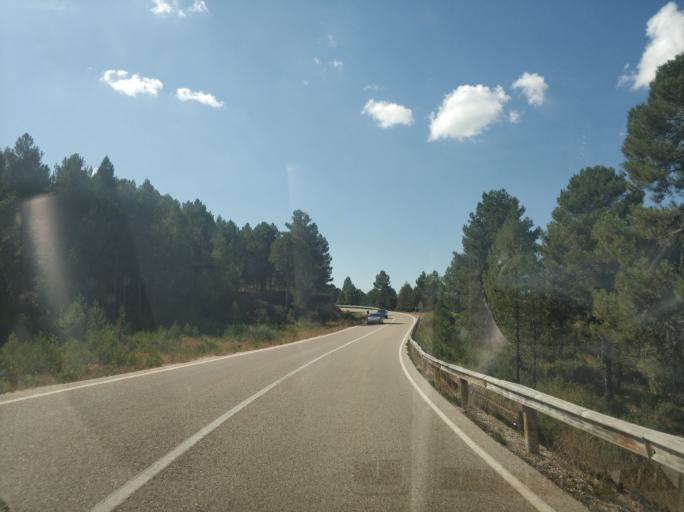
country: ES
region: Castille and Leon
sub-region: Provincia de Soria
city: Herrera de Soria
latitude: 41.7564
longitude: -3.0397
